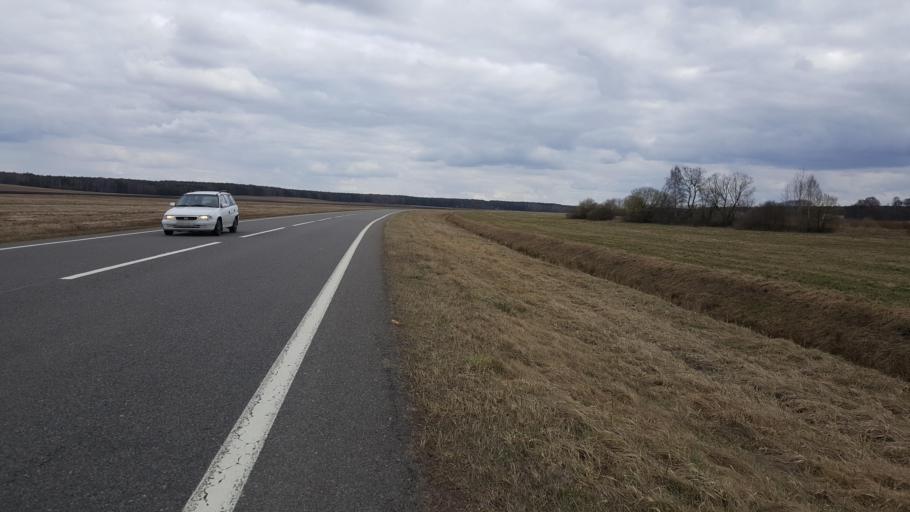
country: BY
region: Brest
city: Kamyanyuki
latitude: 52.4932
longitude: 23.7858
